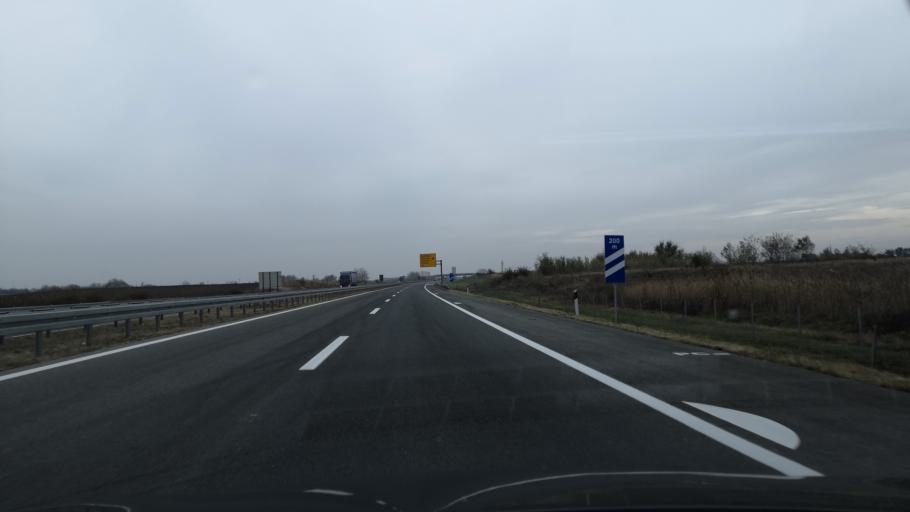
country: RS
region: Autonomna Pokrajina Vojvodina
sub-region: Severnobacki Okrug
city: Mali Igos
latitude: 45.6355
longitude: 19.7100
